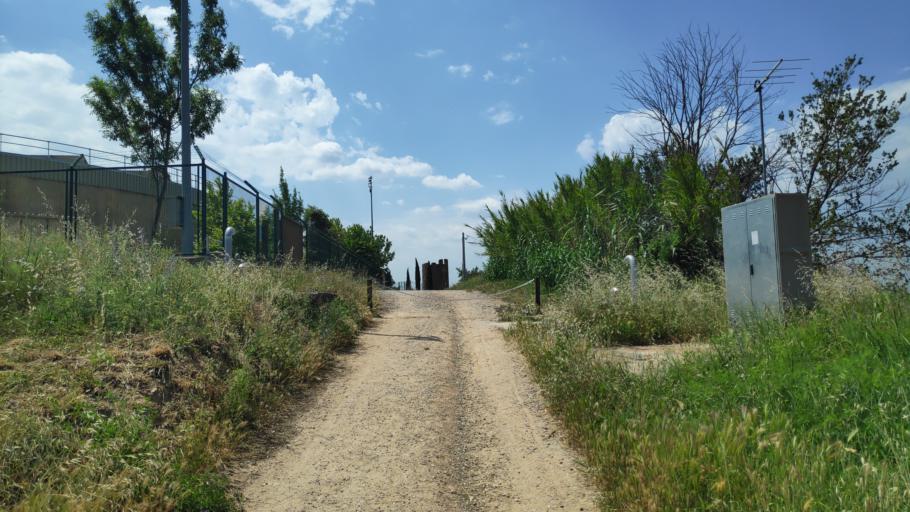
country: ES
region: Catalonia
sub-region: Provincia de Barcelona
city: Les Franqueses del Valles
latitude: 41.6152
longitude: 2.2999
